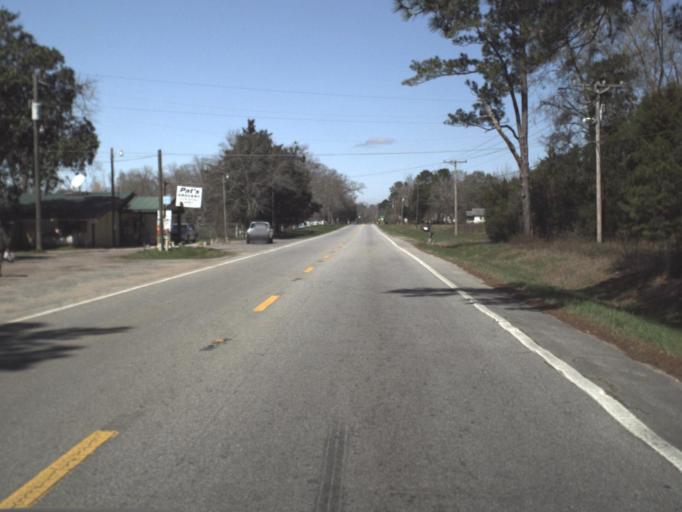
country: US
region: Florida
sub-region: Gadsden County
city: Gretna
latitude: 30.6535
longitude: -84.6030
